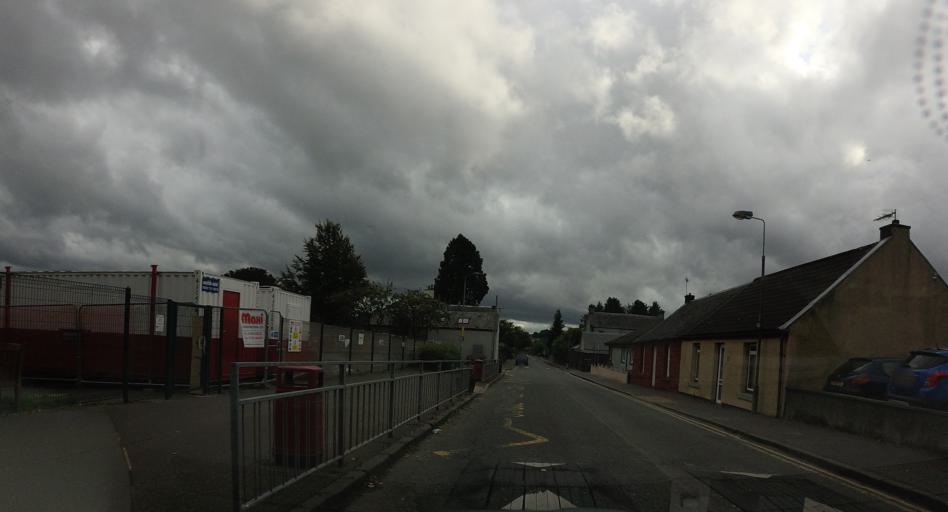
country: GB
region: Scotland
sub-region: Clackmannanshire
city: Alva
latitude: 56.1512
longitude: -3.7982
